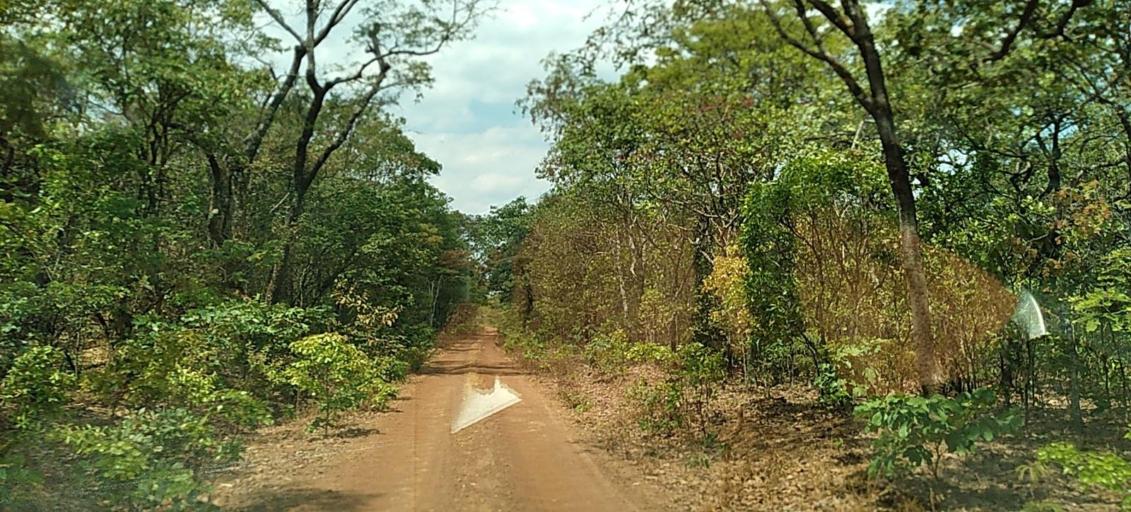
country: ZM
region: Copperbelt
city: Chililabombwe
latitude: -12.4539
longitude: 27.6076
